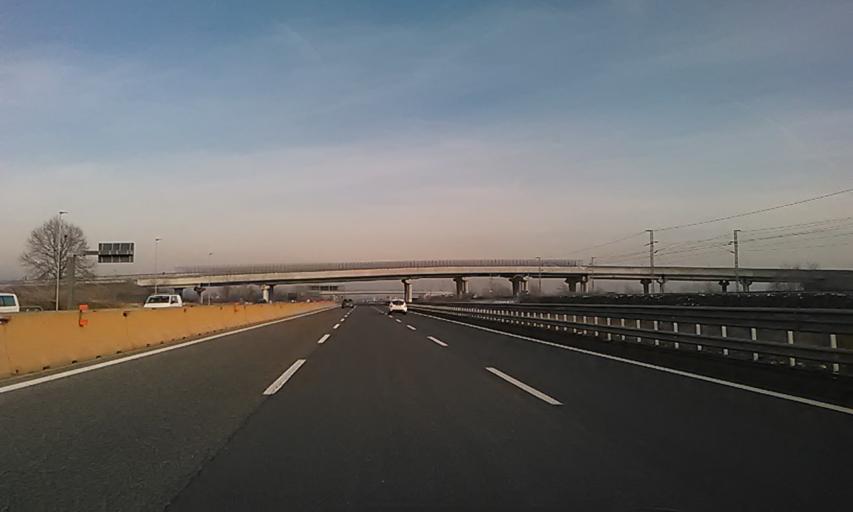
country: IT
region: Piedmont
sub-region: Provincia di Vercelli
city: Villarboit
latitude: 45.4573
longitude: 8.3487
